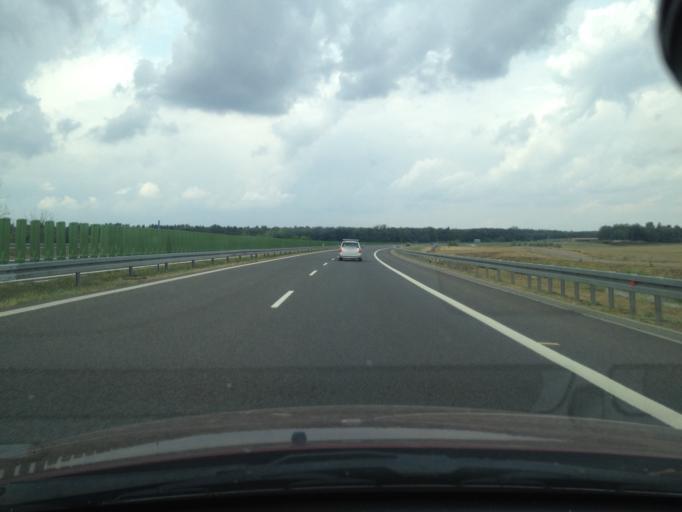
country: PL
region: West Pomeranian Voivodeship
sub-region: Powiat mysliborski
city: Mysliborz
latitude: 52.9866
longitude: 14.8742
